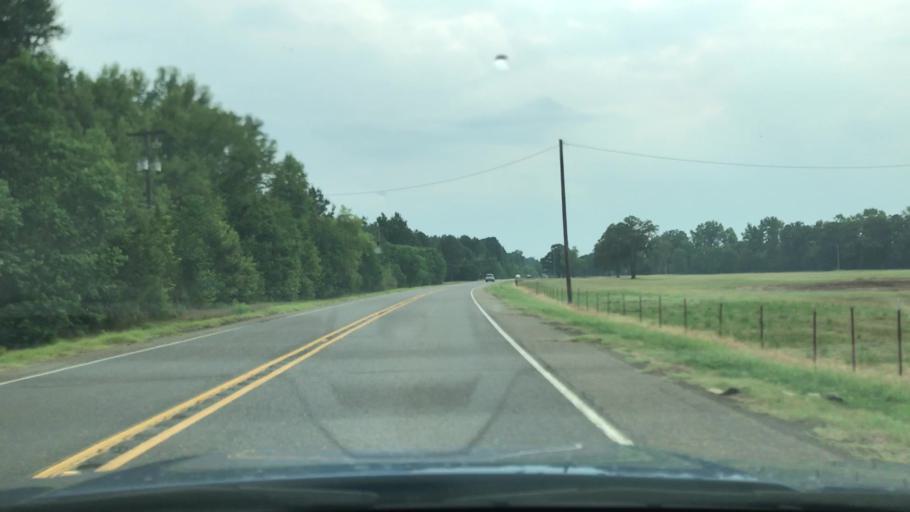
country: US
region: Texas
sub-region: Harrison County
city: Waskom
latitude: 32.4614
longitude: -94.0280
